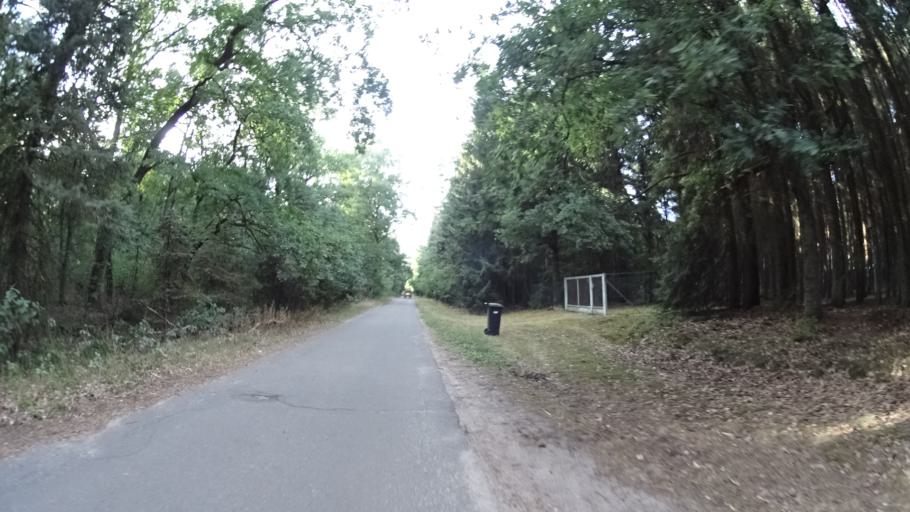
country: DE
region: Lower Saxony
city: Handeloh
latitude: 53.2349
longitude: 9.8667
